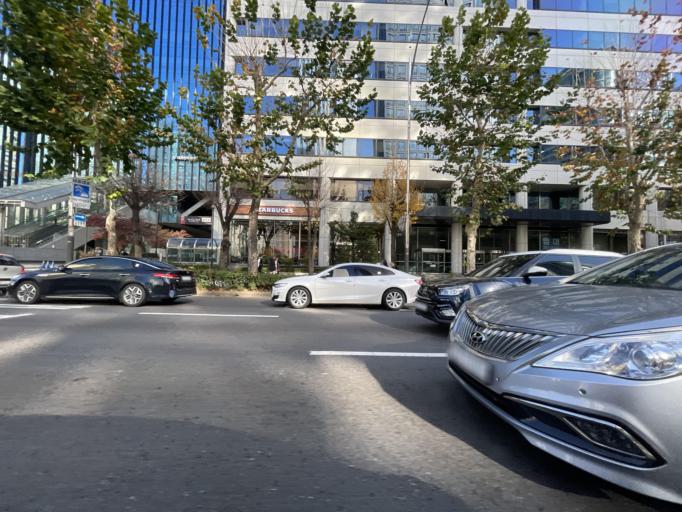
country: KR
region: Seoul
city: Seoul
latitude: 37.5429
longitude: 126.9504
